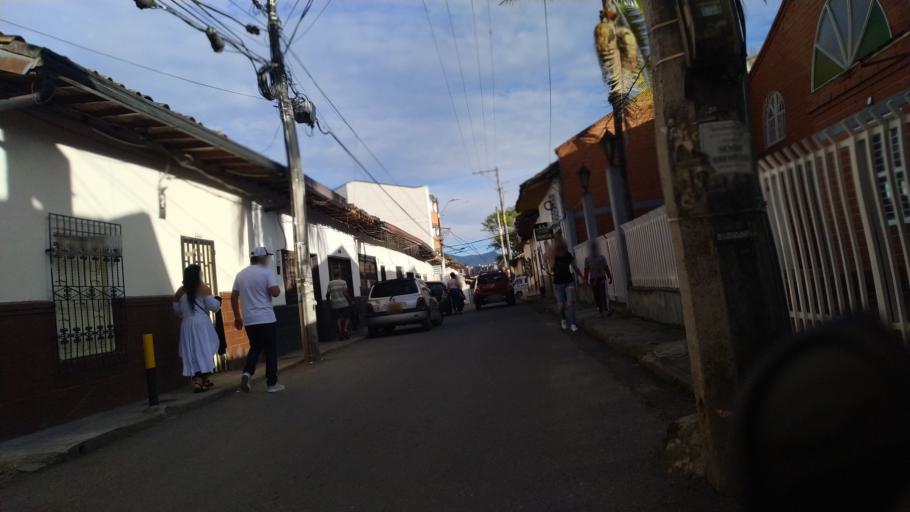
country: CO
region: Antioquia
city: Rionegro
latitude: 6.1512
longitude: -75.3754
